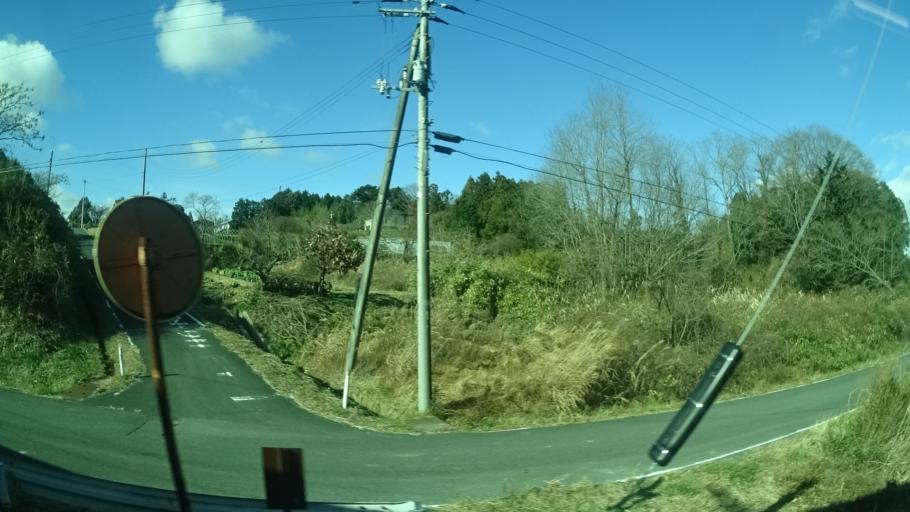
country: JP
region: Miyagi
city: Marumori
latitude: 37.8494
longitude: 140.9262
